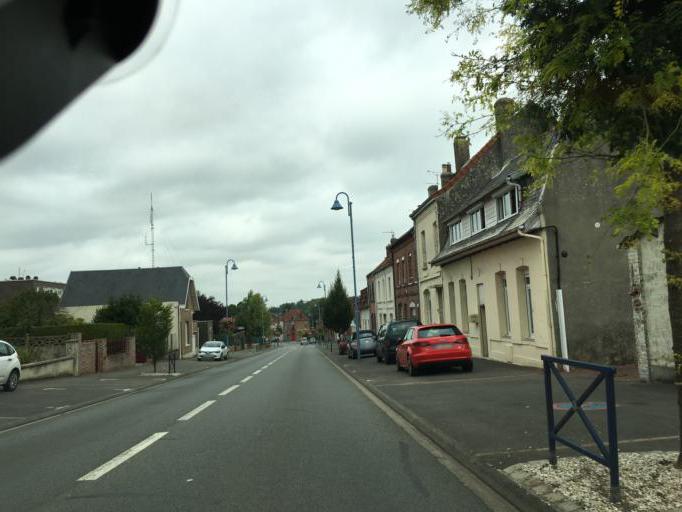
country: FR
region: Nord-Pas-de-Calais
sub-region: Departement du Pas-de-Calais
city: Saint-Pol-sur-Ternoise
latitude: 50.3750
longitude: 2.3330
